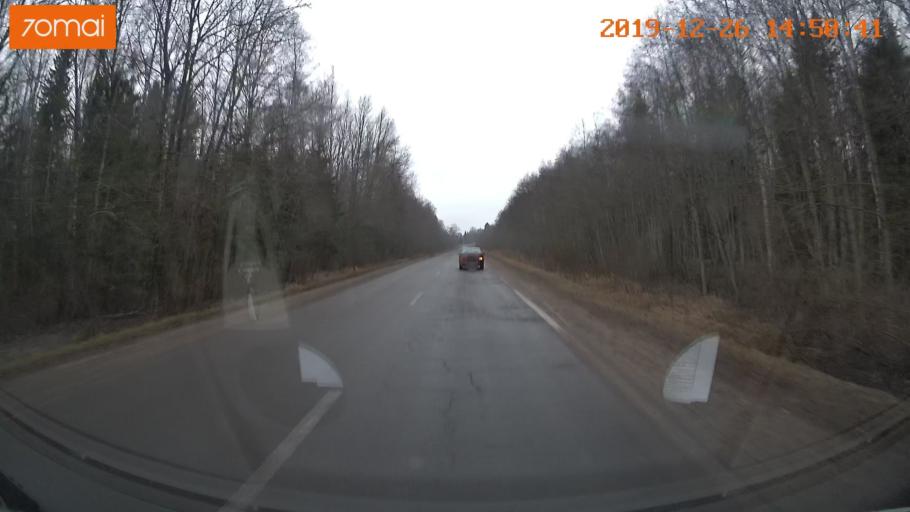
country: RU
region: Jaroslavl
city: Poshekhon'ye
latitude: 58.3301
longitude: 38.9217
